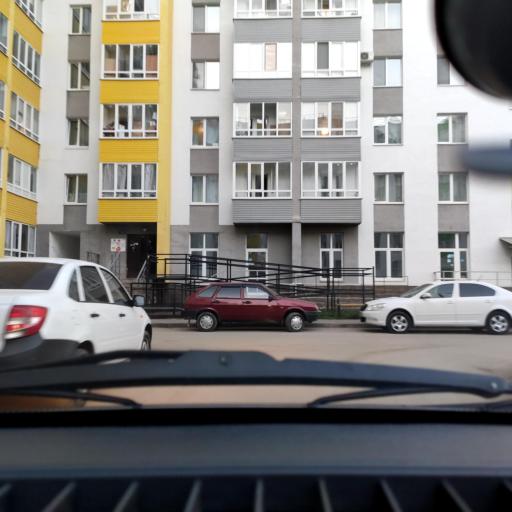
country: RU
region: Bashkortostan
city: Ufa
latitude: 54.6860
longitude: 55.9811
